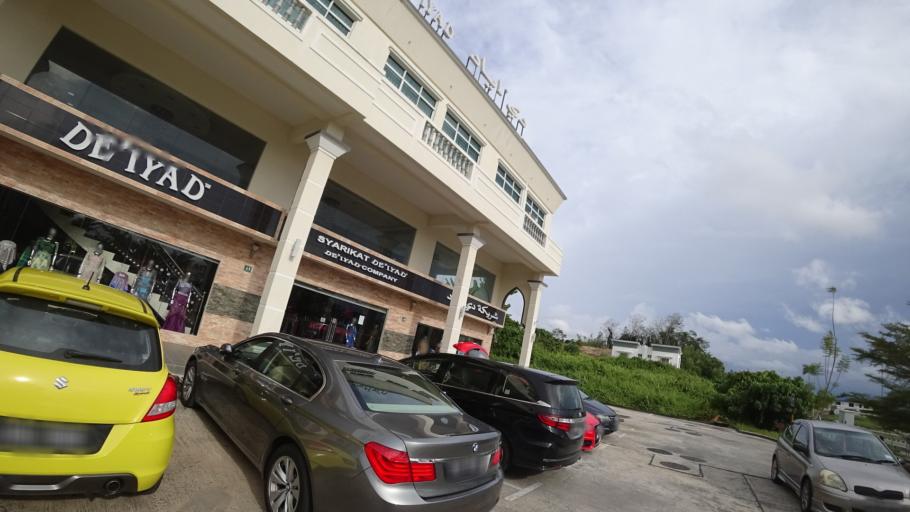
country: BN
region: Brunei and Muara
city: Bandar Seri Begawan
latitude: 4.8884
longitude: 114.8582
